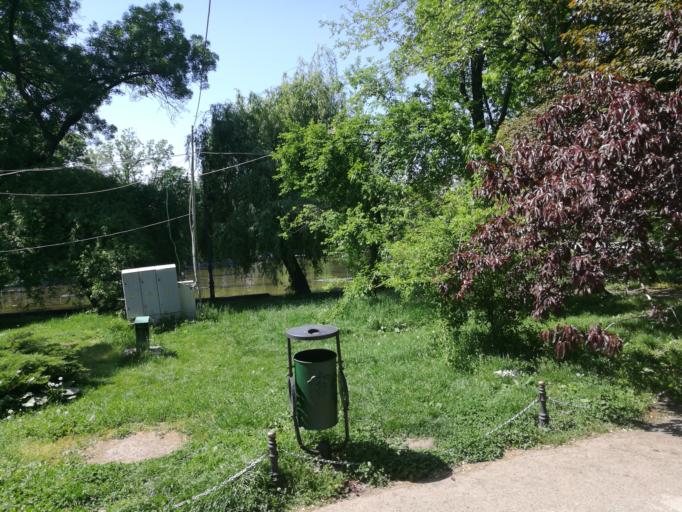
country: RO
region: Bucuresti
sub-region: Municipiul Bucuresti
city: Bucuresti
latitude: 44.4354
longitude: 26.0926
